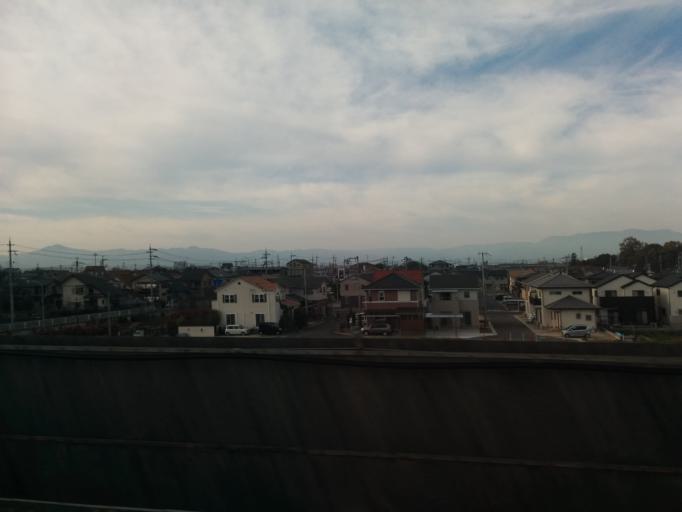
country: JP
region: Shiga Prefecture
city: Moriyama
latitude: 35.0569
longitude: 136.0173
